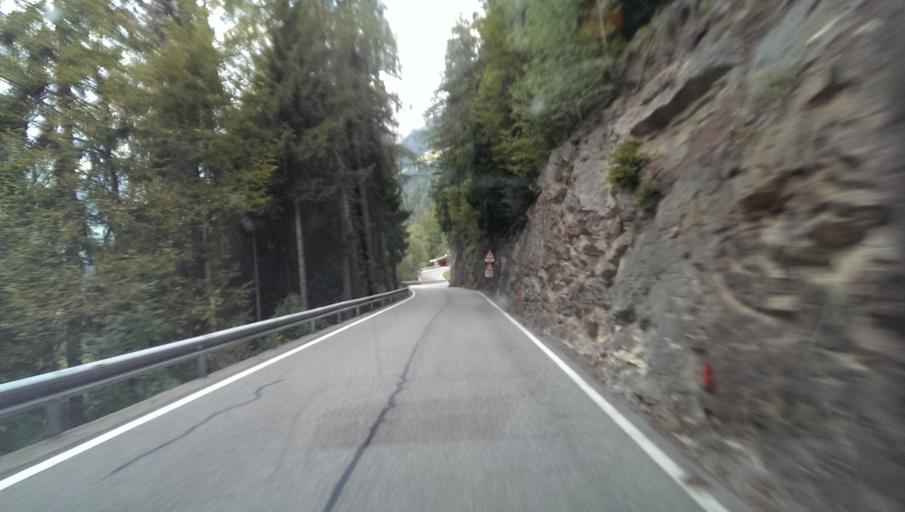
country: IT
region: Trentino-Alto Adige
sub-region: Bolzano
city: San Leonardo in Passiria
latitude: 46.8202
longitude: 11.2489
